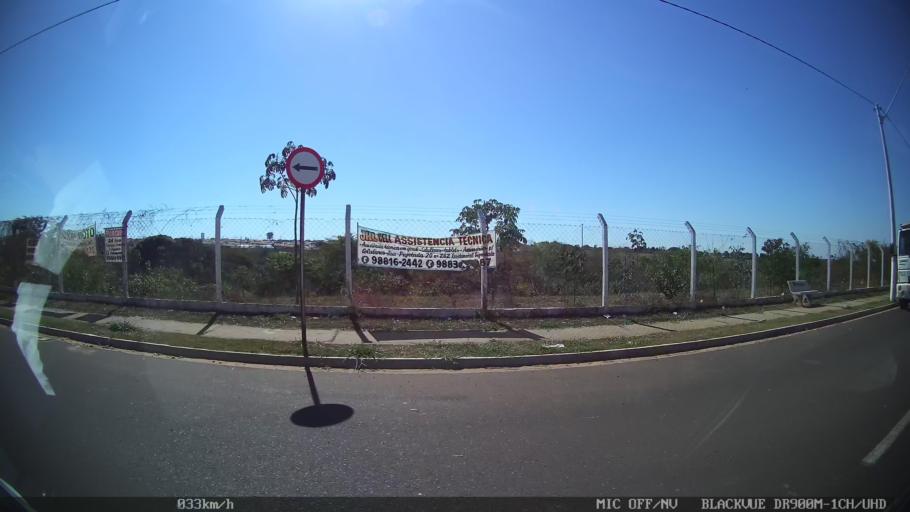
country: BR
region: Sao Paulo
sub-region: Sao Jose Do Rio Preto
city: Sao Jose do Rio Preto
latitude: -20.7592
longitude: -49.4347
